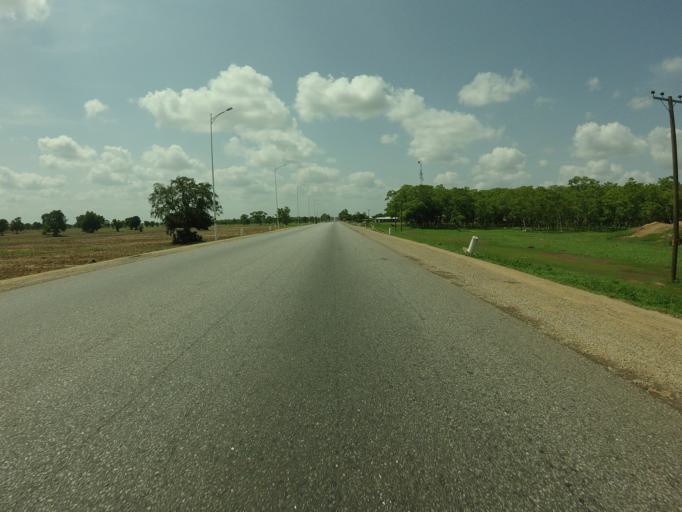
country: GH
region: Northern
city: Savelugu
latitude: 9.5435
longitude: -0.8386
